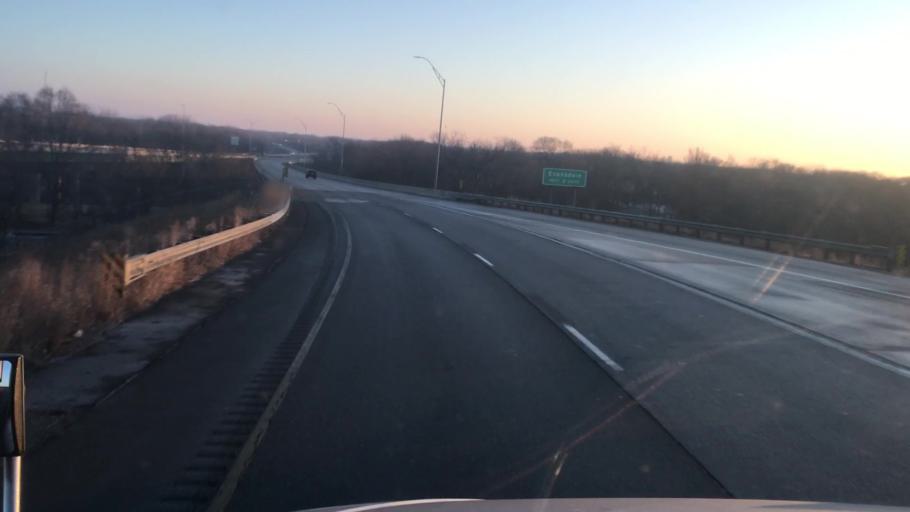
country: US
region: Iowa
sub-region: Black Hawk County
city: Evansdale
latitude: 42.4543
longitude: -92.3087
